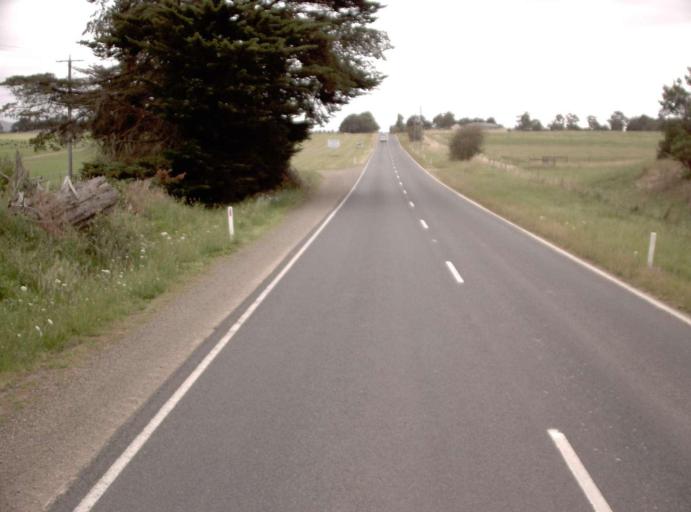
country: AU
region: Victoria
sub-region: Yarra Ranges
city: Lilydale
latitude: -37.7128
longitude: 145.3807
